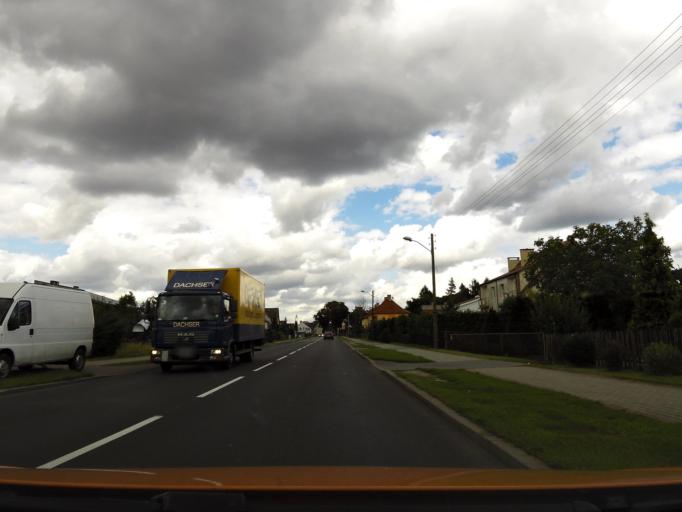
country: PL
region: West Pomeranian Voivodeship
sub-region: Powiat gryficki
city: Ploty
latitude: 53.7971
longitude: 15.2579
